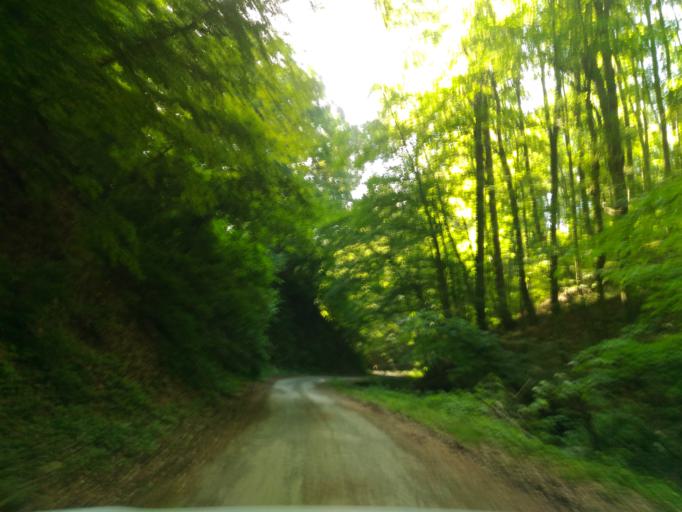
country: HU
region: Baranya
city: Hosszuheteny
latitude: 46.2238
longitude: 18.3315
